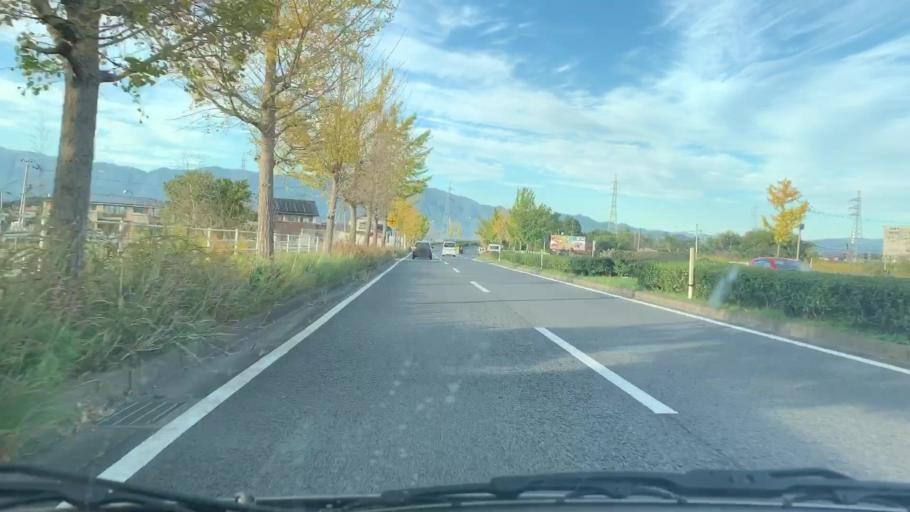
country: JP
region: Saga Prefecture
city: Saga-shi
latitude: 33.2522
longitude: 130.1989
